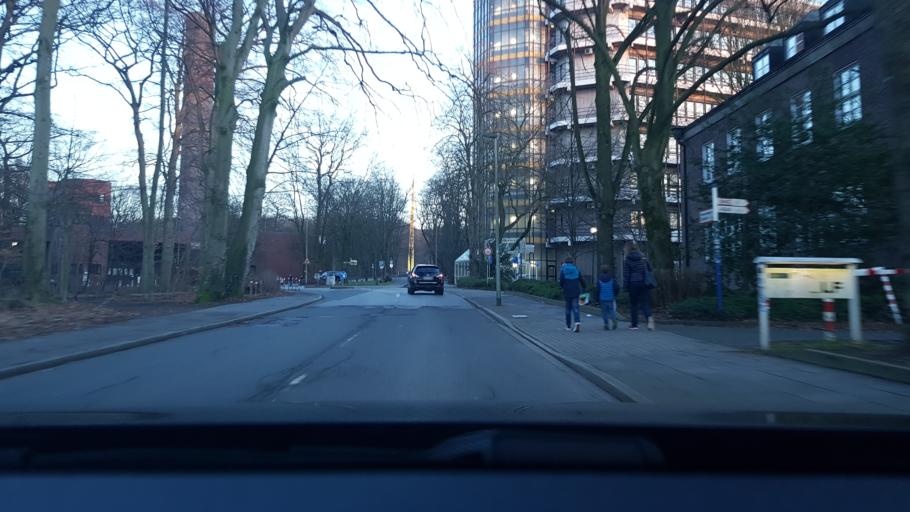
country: DE
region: North Rhine-Westphalia
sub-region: Regierungsbezirk Dusseldorf
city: Duisburg
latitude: 51.4286
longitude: 6.8002
